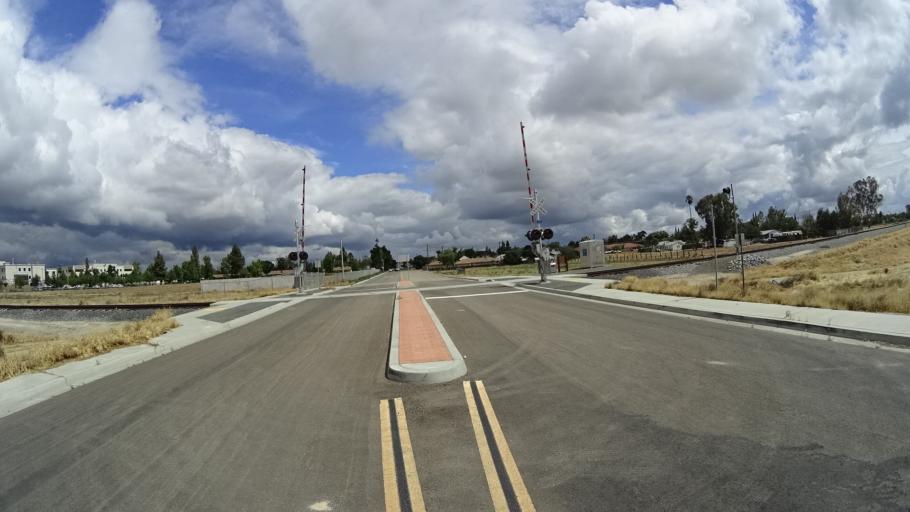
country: US
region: California
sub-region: Kings County
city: Hanford
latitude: 36.3218
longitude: -119.6642
